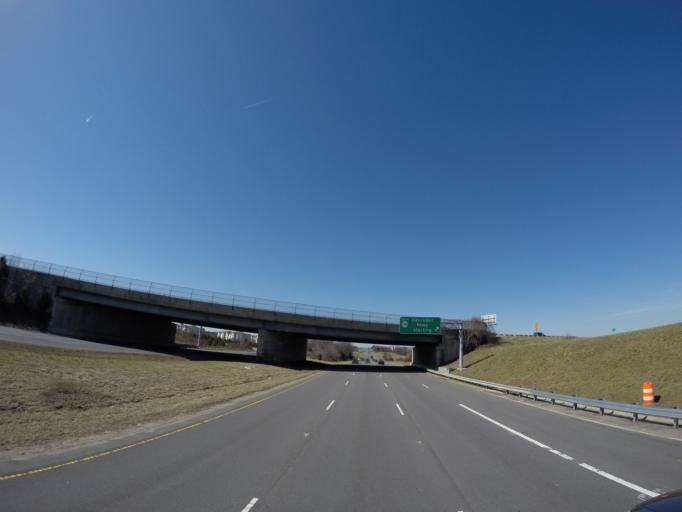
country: US
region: Virginia
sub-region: Loudoun County
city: Countryside
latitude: 39.0301
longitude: -77.4008
